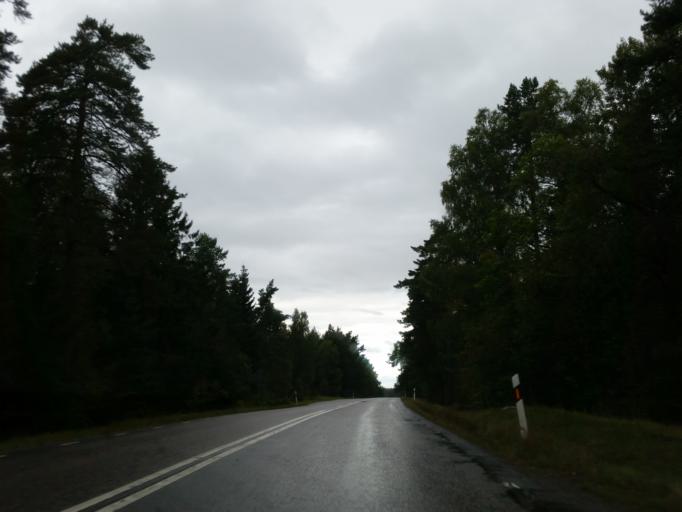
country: SE
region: Uppsala
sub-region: Habo Kommun
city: Balsta
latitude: 59.6441
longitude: 17.4351
